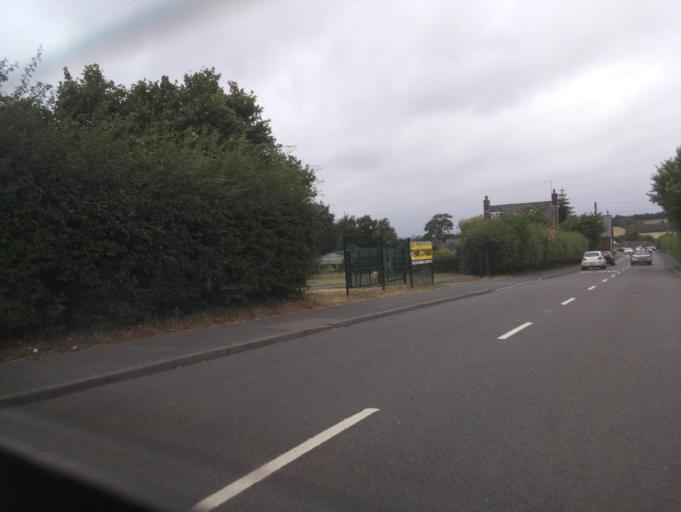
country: GB
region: England
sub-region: Derbyshire
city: Swadlincote
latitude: 52.7850
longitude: -1.5183
